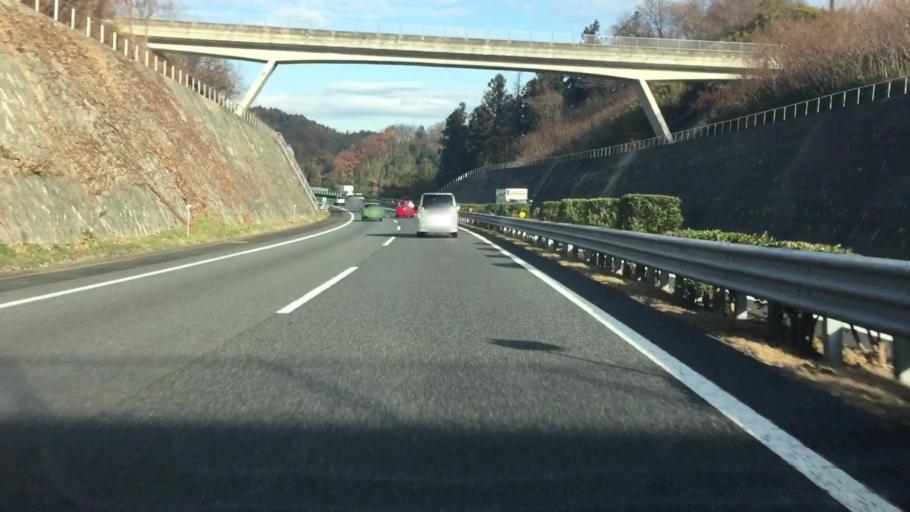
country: JP
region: Gunma
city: Tomioka
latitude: 36.2556
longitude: 138.8186
